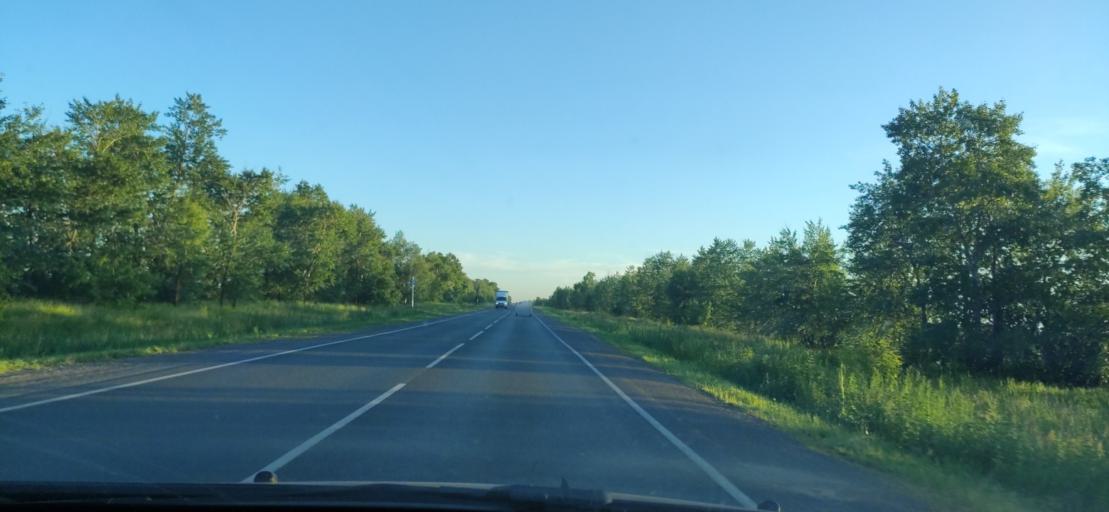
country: RU
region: Ulyanovsk
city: Cherdakly
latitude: 54.4071
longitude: 48.8722
